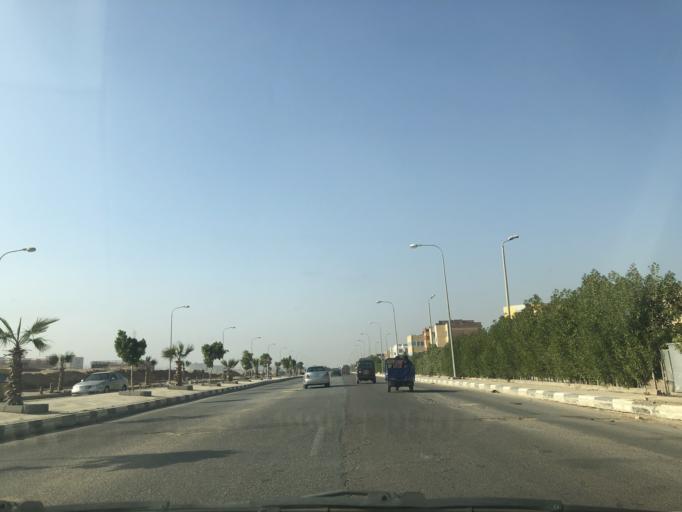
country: EG
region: Al Jizah
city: Madinat Sittah Uktubar
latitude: 29.9275
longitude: 31.0509
